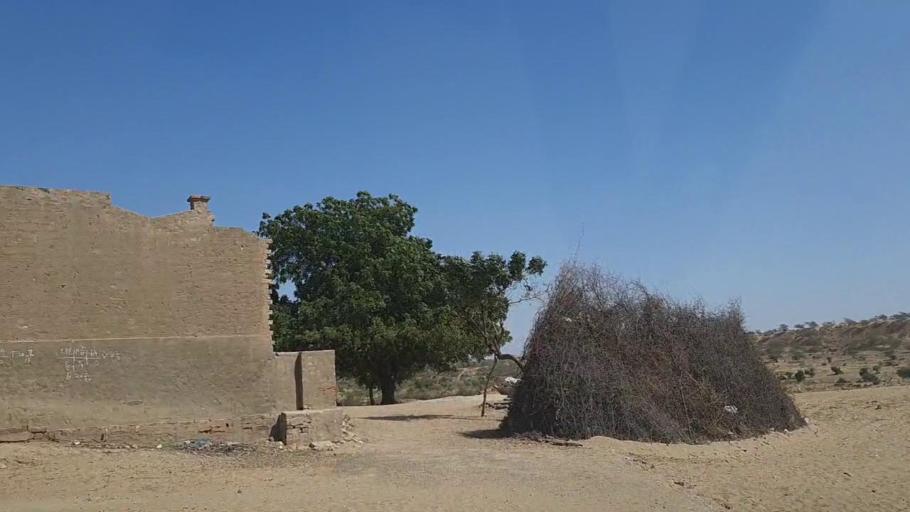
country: PK
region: Sindh
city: Mithi
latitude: 24.8348
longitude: 69.6507
